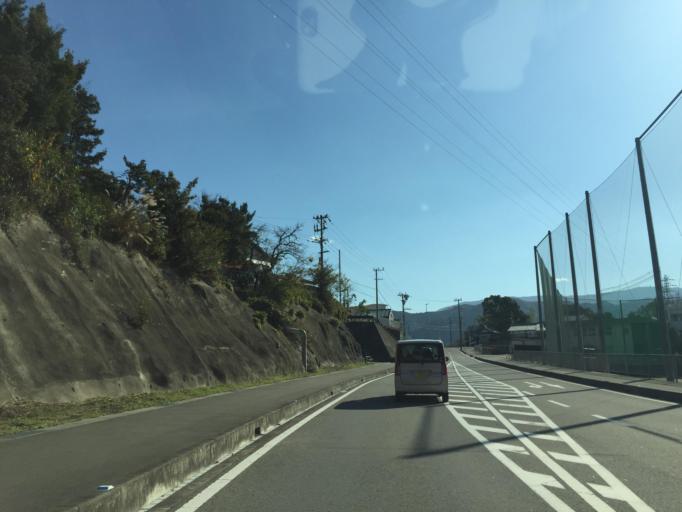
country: JP
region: Wakayama
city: Iwade
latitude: 34.1650
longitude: 135.3053
